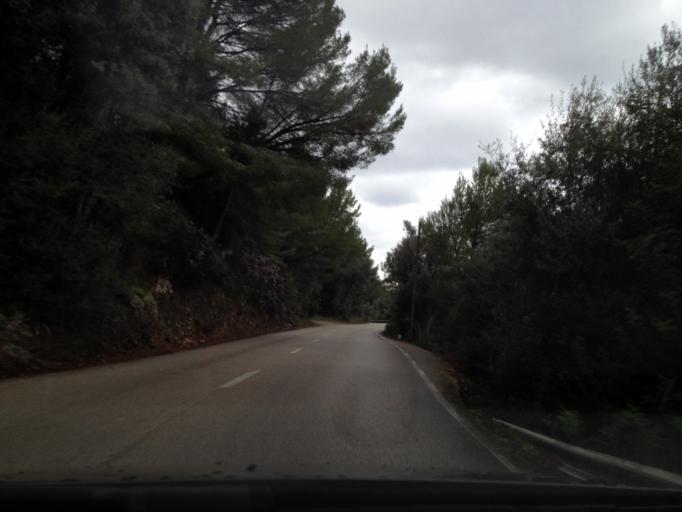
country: ES
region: Balearic Islands
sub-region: Illes Balears
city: Deia
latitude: 39.7673
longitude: 2.6607
